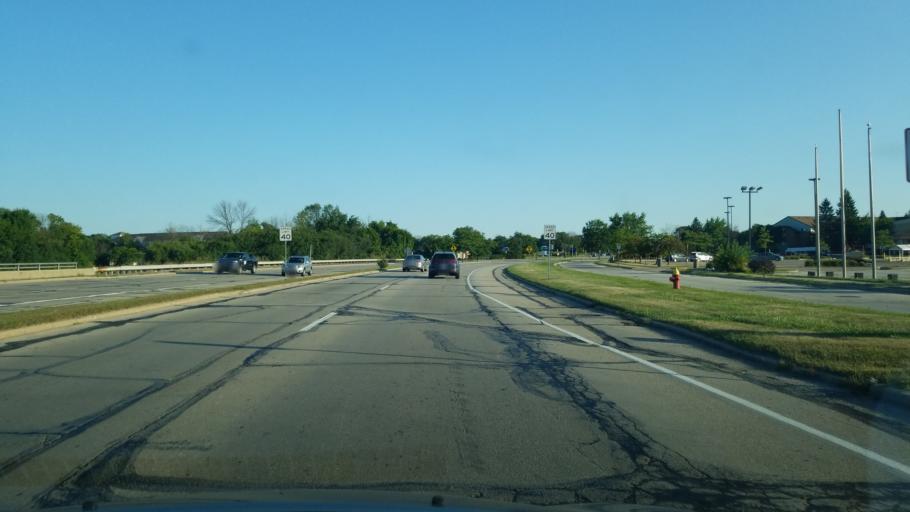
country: US
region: Wisconsin
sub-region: Milwaukee County
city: Brown Deer
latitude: 43.1831
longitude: -87.9635
